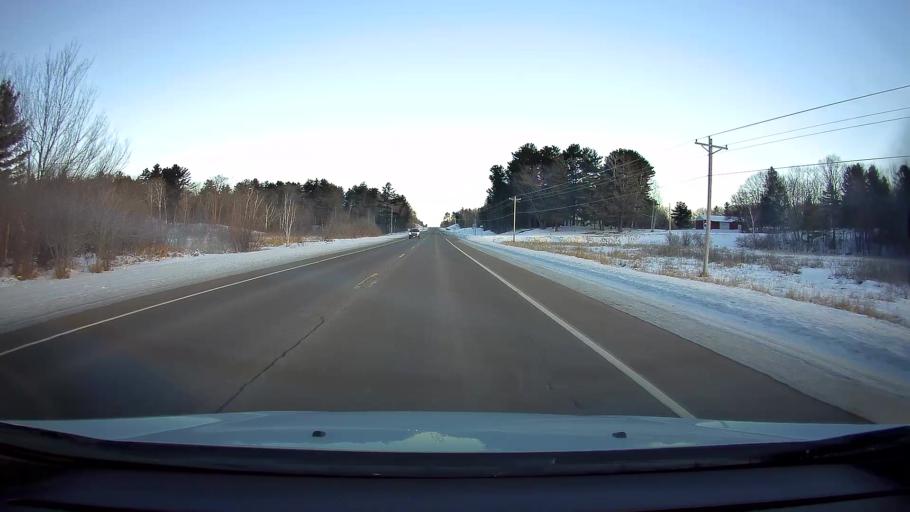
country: US
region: Wisconsin
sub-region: Barron County
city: Cumberland
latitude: 45.5783
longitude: -92.0175
